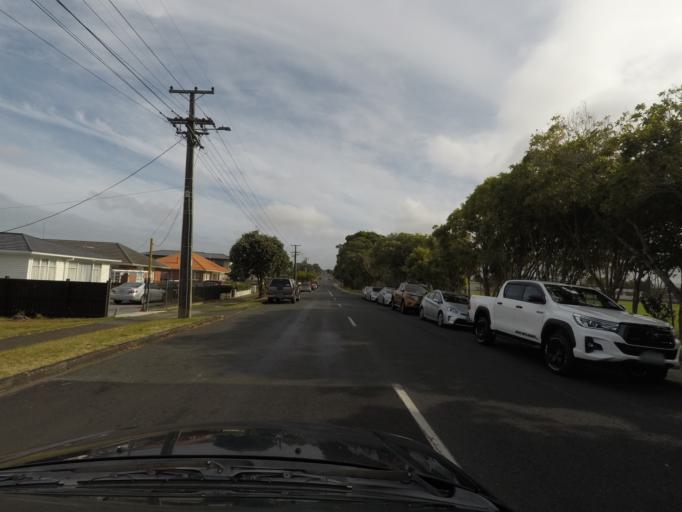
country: NZ
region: Auckland
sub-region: Auckland
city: Waitakere
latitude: -36.8981
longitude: 174.6677
